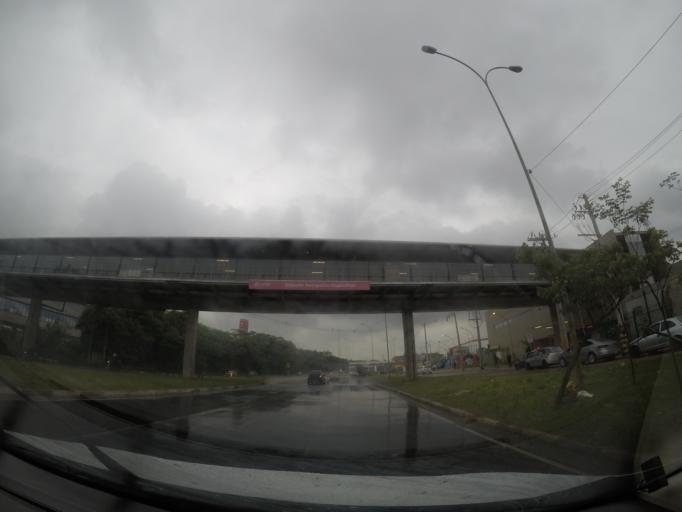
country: BR
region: Sao Paulo
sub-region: Guarulhos
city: Guarulhos
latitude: -23.4323
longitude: -46.4947
